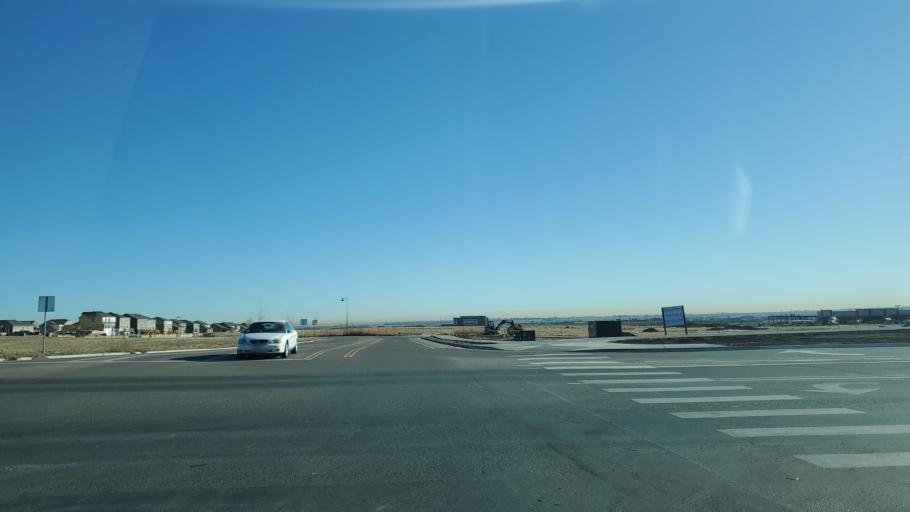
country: US
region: Colorado
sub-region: Boulder County
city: Erie
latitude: 40.0041
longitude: -105.0054
